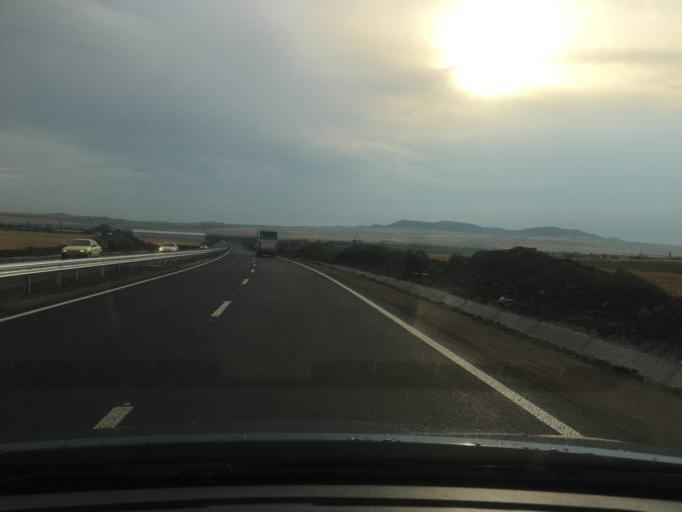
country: BG
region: Burgas
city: Aheloy
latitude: 42.6565
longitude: 27.6543
